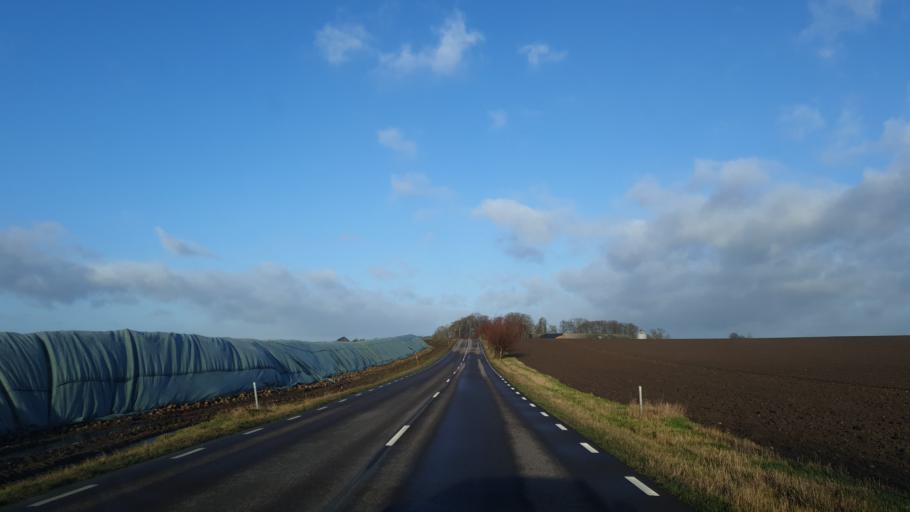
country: SE
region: Skane
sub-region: Vellinge Kommun
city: Vellinge
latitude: 55.4935
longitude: 13.0270
